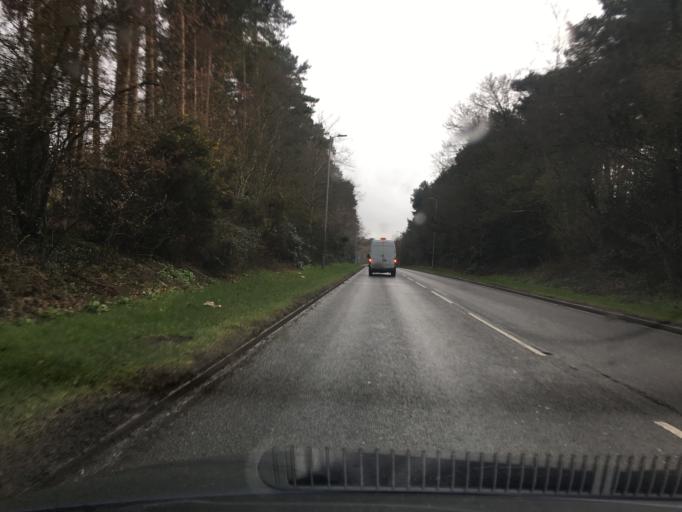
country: GB
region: England
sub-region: Bracknell Forest
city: Bracknell
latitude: 51.3945
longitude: -0.7656
